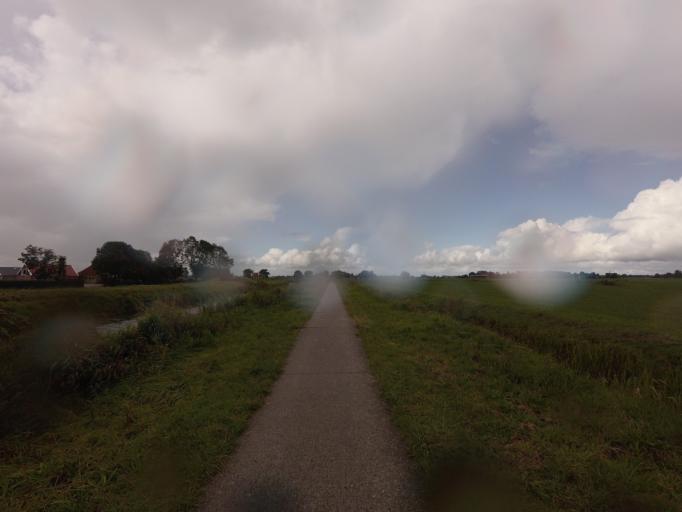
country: NL
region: Friesland
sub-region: Gemeente Boarnsterhim
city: Wergea
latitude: 53.1483
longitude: 5.8308
